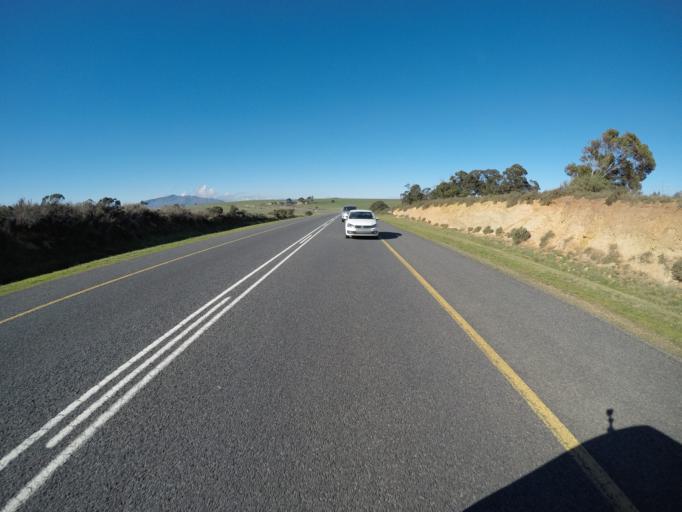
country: ZA
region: Western Cape
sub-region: Overberg District Municipality
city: Caledon
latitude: -34.2242
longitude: 19.2893
